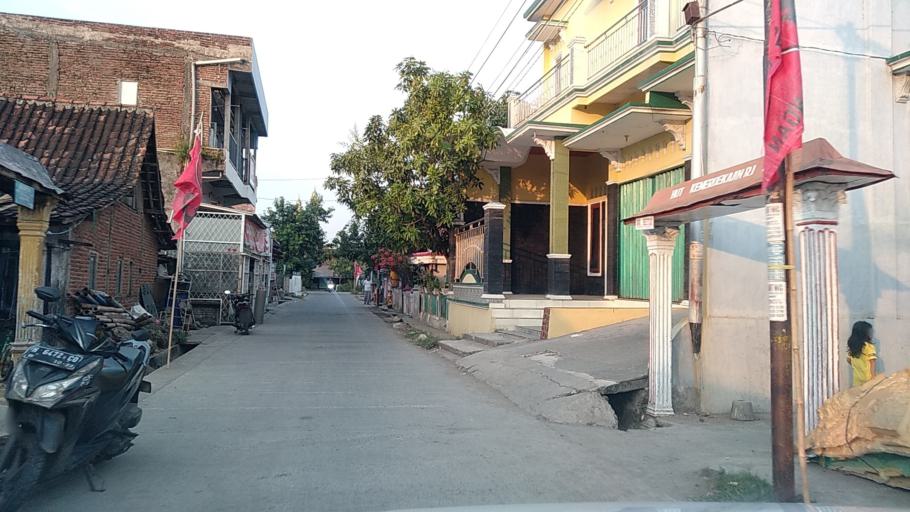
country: ID
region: Central Java
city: Semarang
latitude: -6.9564
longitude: 110.3139
